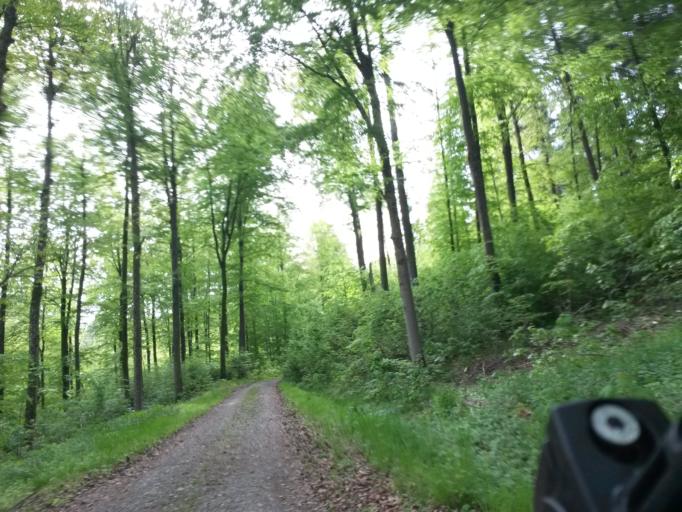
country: DE
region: Baden-Wuerttemberg
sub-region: Tuebingen Region
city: Baindt
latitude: 47.8906
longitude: 9.6701
